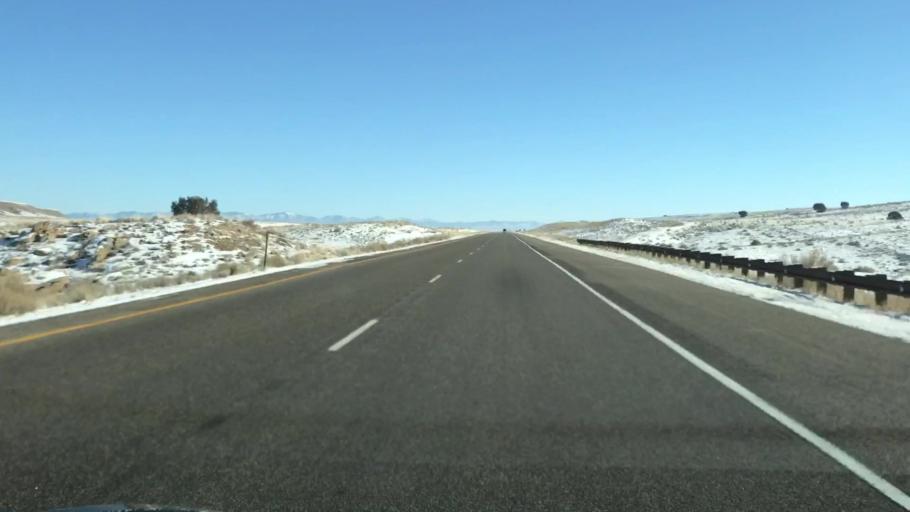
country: US
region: Colorado
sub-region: Mesa County
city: Loma
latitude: 39.2229
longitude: -108.9414
